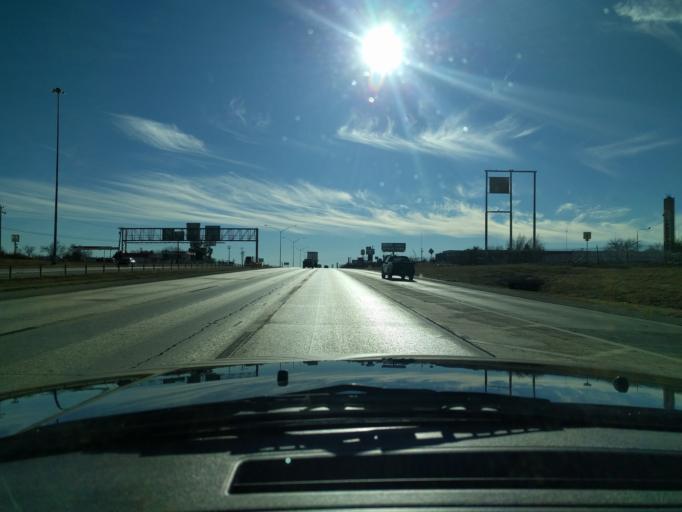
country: US
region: Oklahoma
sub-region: Oklahoma County
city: Edmond
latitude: 35.5911
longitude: -97.4353
